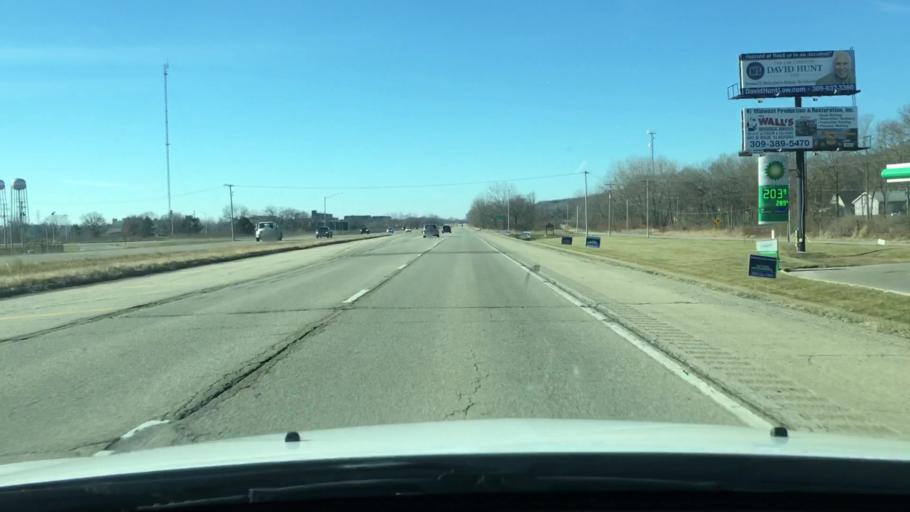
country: US
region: Illinois
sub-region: Peoria County
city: Glasford
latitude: 40.5659
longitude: -89.7289
